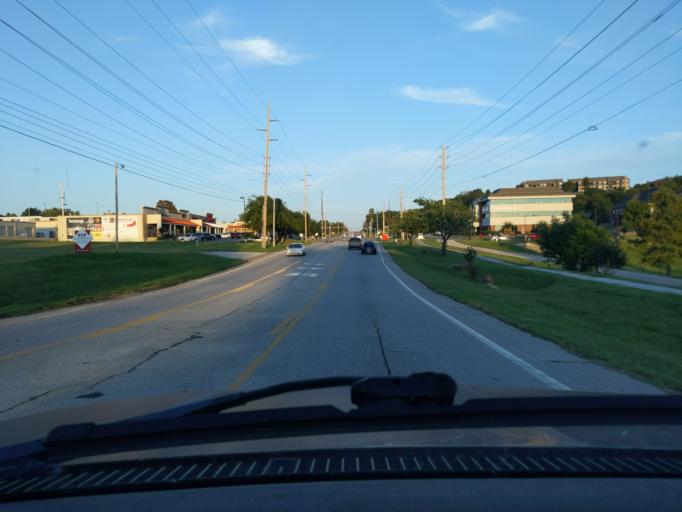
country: US
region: Oklahoma
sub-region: Tulsa County
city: Jenks
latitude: 36.0463
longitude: -95.9256
